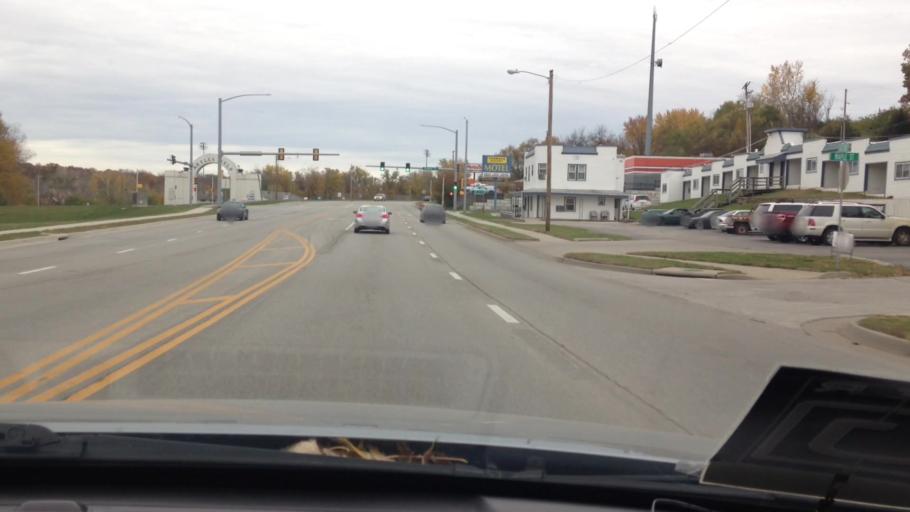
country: US
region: Kansas
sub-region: Leavenworth County
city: Leavenworth
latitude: 39.3047
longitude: -94.9097
